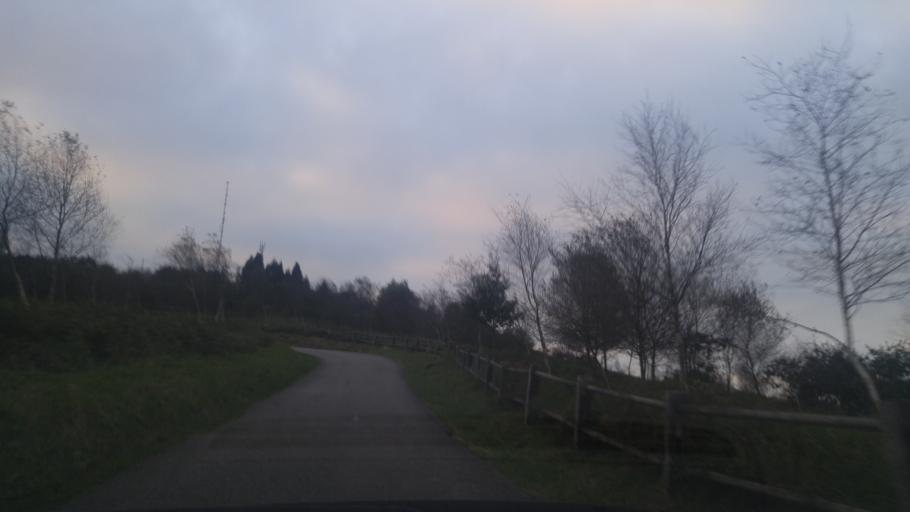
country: ES
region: Asturias
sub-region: Province of Asturias
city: Oviedo
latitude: 43.3845
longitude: -5.8600
